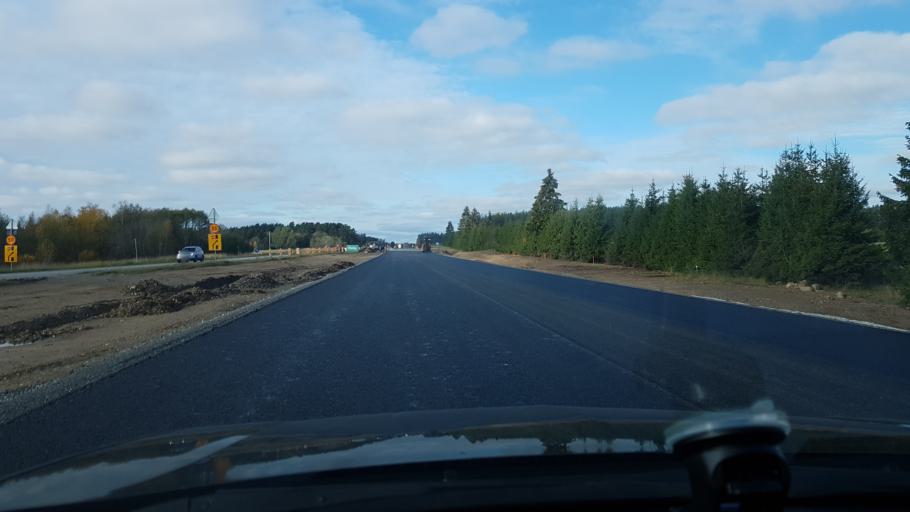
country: EE
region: Laeaene-Virumaa
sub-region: Kadrina vald
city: Kadrina
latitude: 59.4442
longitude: 26.0977
